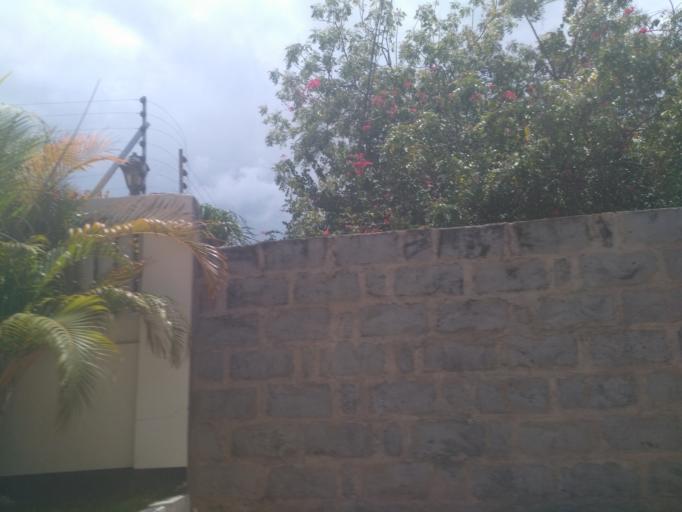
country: TZ
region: Dar es Salaam
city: Magomeni
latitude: -6.7516
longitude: 39.2747
